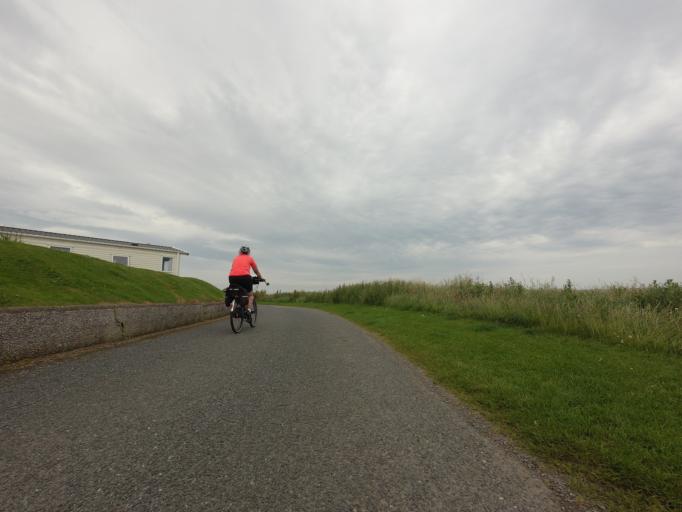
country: GB
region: Scotland
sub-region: Aberdeenshire
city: Whitehills
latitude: 57.6809
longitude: -2.5705
